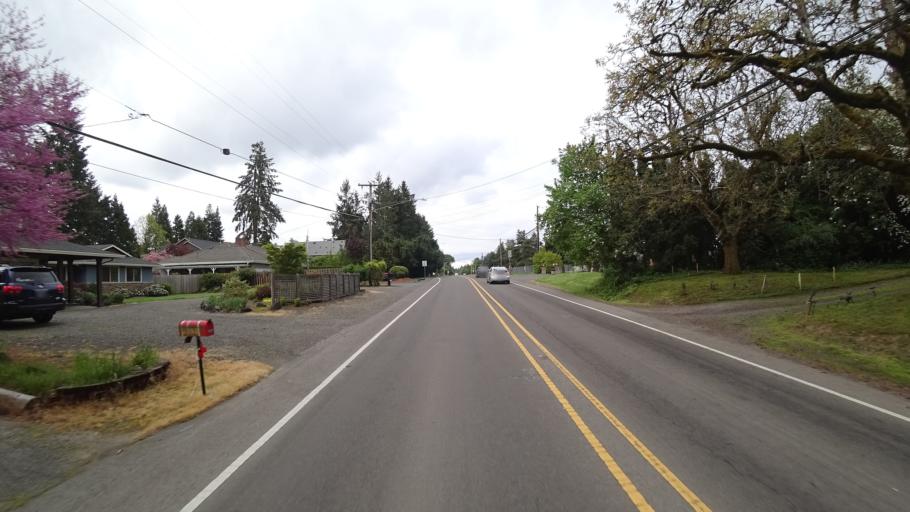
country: US
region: Oregon
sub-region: Washington County
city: Hillsboro
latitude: 45.5453
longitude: -122.9797
